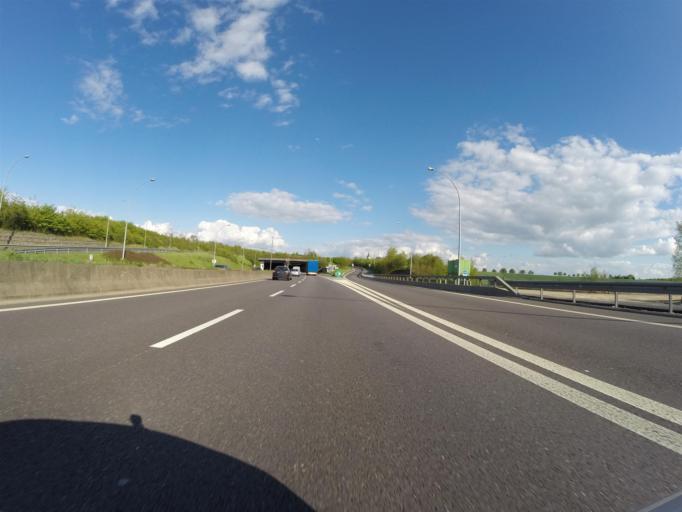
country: LU
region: Luxembourg
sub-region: Canton d'Esch-sur-Alzette
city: Frisange
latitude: 49.5077
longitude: 6.1878
